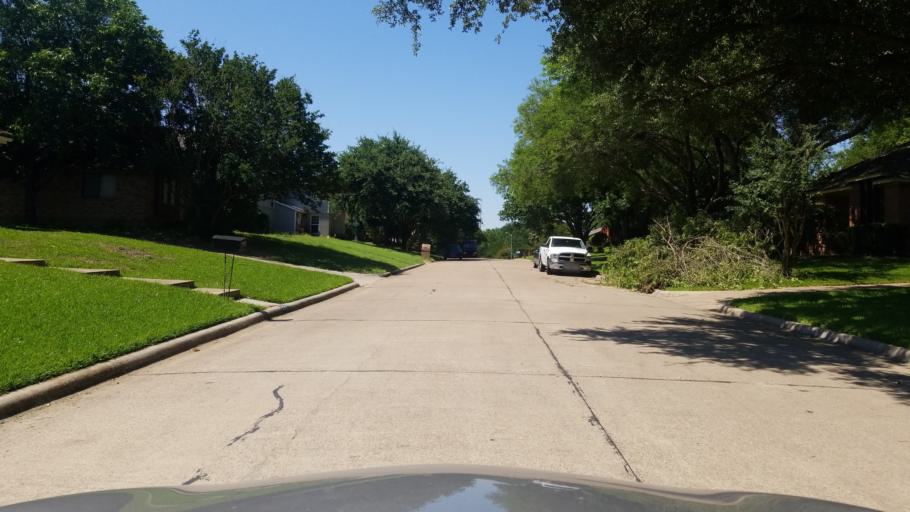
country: US
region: Texas
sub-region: Dallas County
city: Grand Prairie
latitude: 32.6858
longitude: -96.9978
